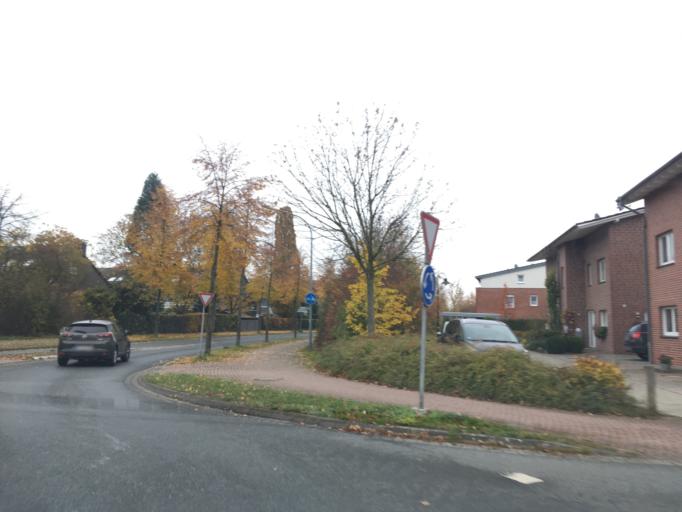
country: DE
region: North Rhine-Westphalia
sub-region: Regierungsbezirk Munster
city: Telgte
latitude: 51.9738
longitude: 7.7796
